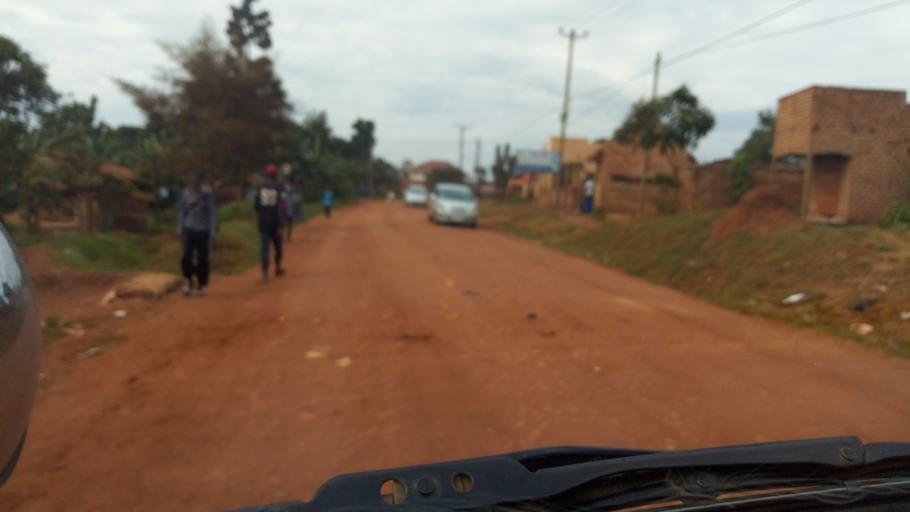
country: UG
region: Central Region
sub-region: Wakiso District
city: Bweyogerere
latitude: 0.3572
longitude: 32.7007
